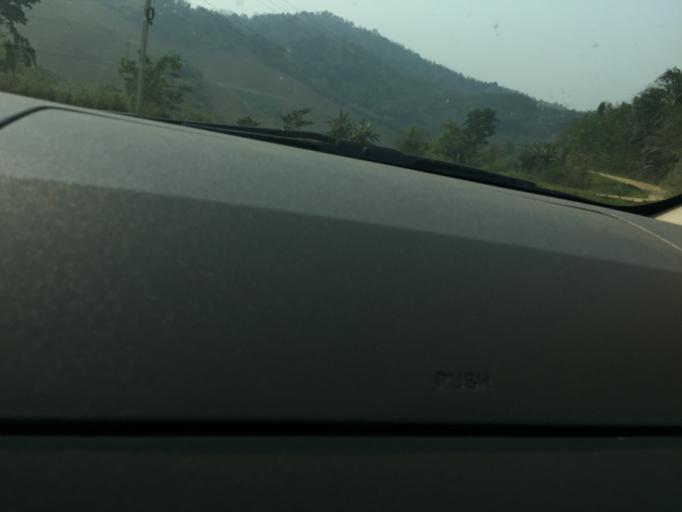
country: TH
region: Phayao
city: Phu Sang
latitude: 19.6098
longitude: 100.5398
